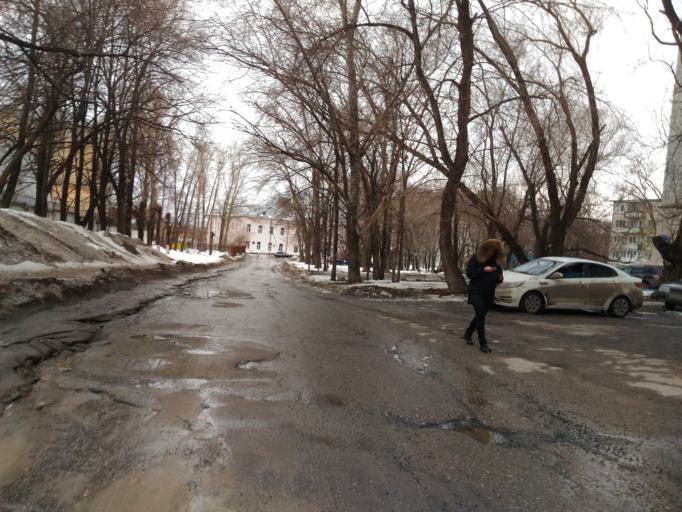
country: RU
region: Ulyanovsk
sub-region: Ulyanovskiy Rayon
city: Ulyanovsk
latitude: 54.3068
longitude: 48.3863
